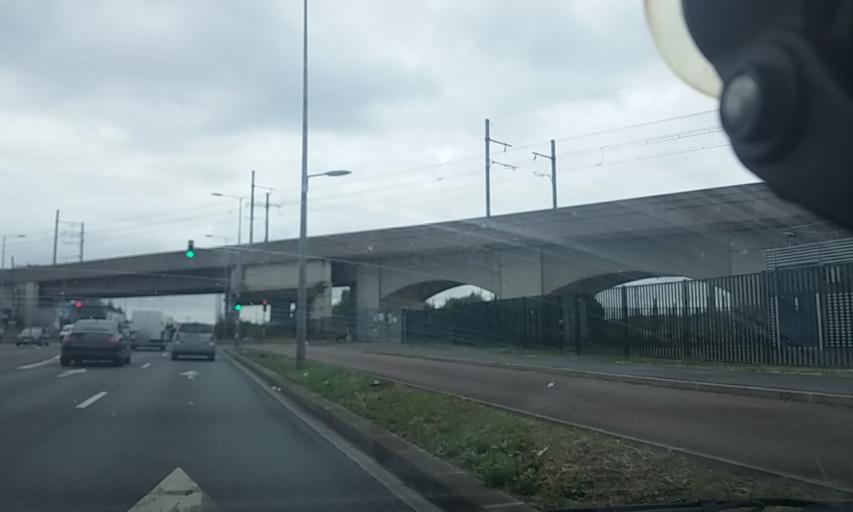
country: FR
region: Ile-de-France
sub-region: Departement du Val-de-Marne
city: Choisy-le-Roi
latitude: 48.7709
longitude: 2.4399
